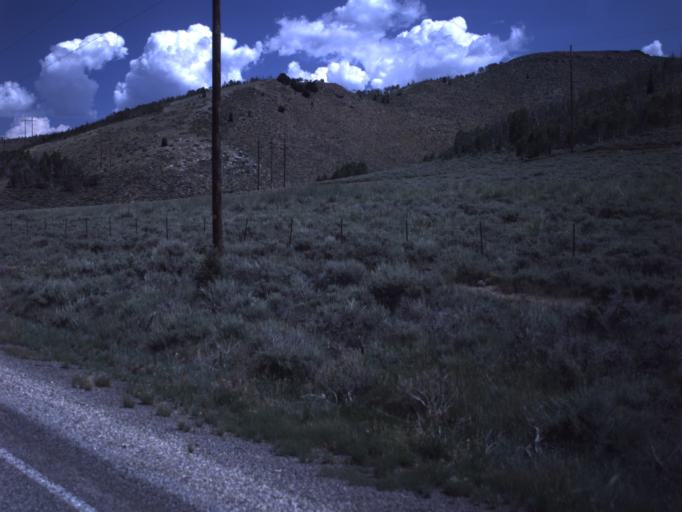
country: US
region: Utah
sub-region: Carbon County
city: Helper
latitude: 39.8132
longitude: -111.1352
